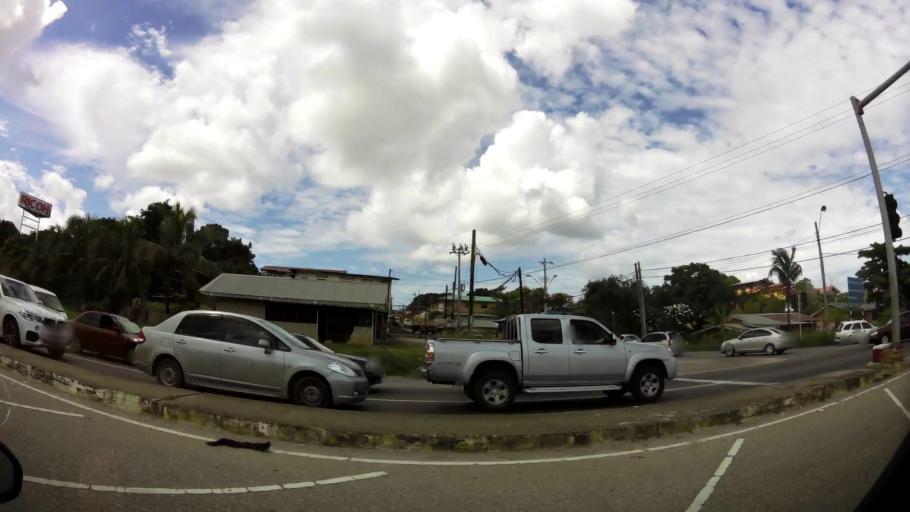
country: TT
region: City of San Fernando
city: Mon Repos
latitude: 10.2854
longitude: -61.4473
